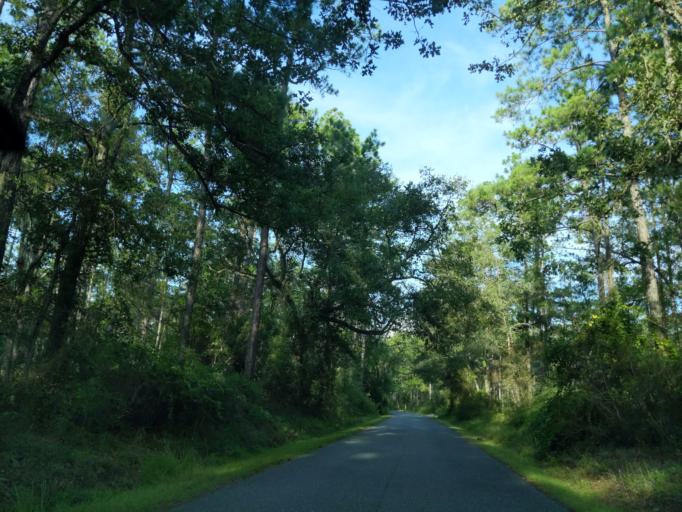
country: US
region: Florida
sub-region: Leon County
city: Woodville
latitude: 30.3448
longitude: -84.3795
